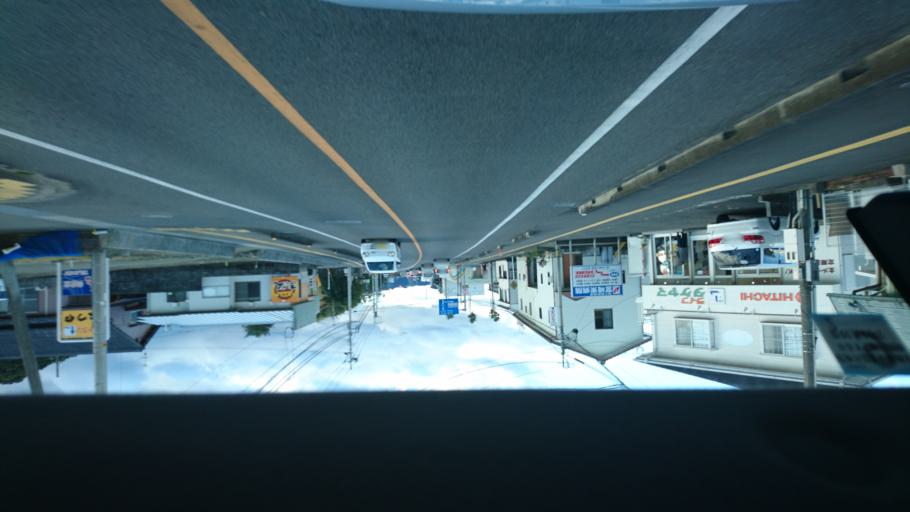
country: JP
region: Miyazaki
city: Miyazaki-shi
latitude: 31.8712
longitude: 131.4318
